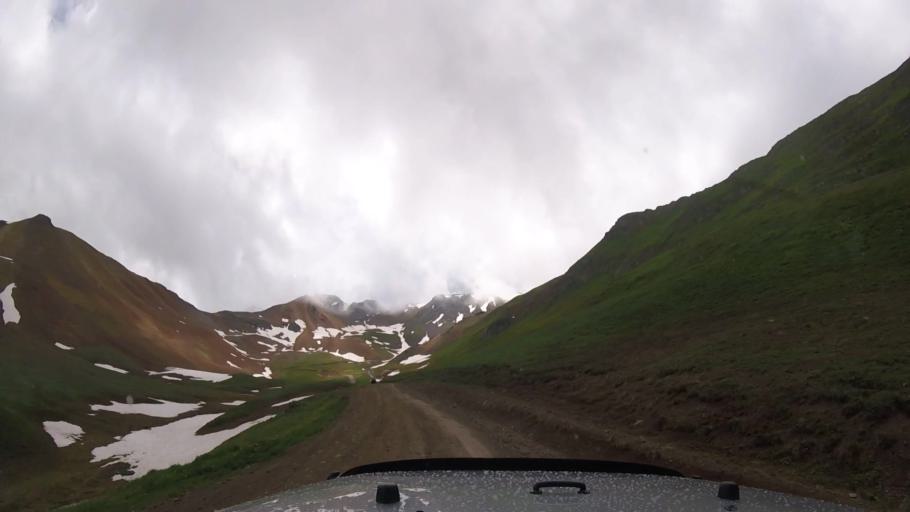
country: US
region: Colorado
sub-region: Ouray County
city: Ouray
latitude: 37.9219
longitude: -107.6119
